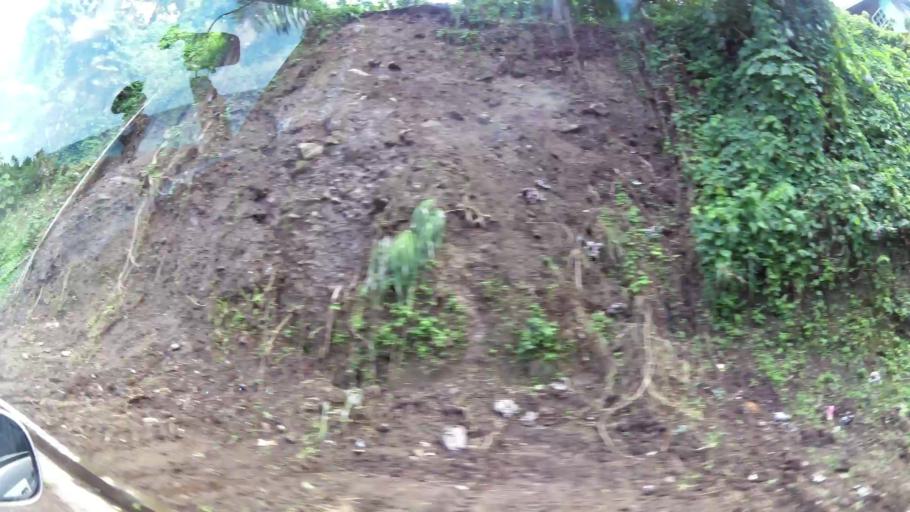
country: GD
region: Saint Mark
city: Victoria
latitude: 12.2019
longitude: -61.7003
